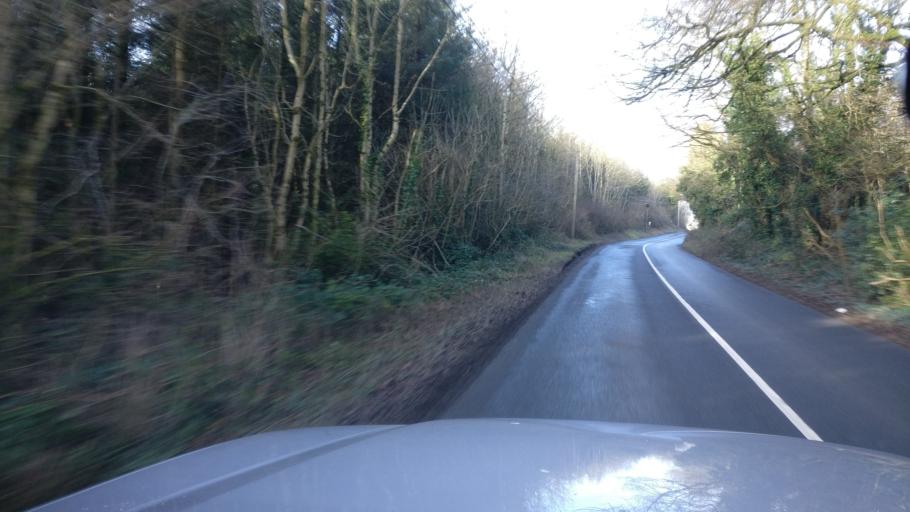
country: IE
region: Leinster
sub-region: Laois
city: Stradbally
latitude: 52.9432
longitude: -7.2000
